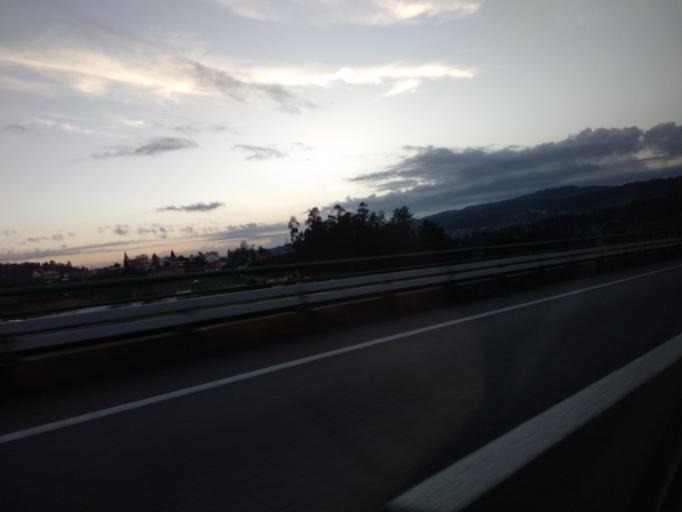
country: PT
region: Braga
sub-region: Braga
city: Oliveira
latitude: 41.4973
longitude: -8.4696
